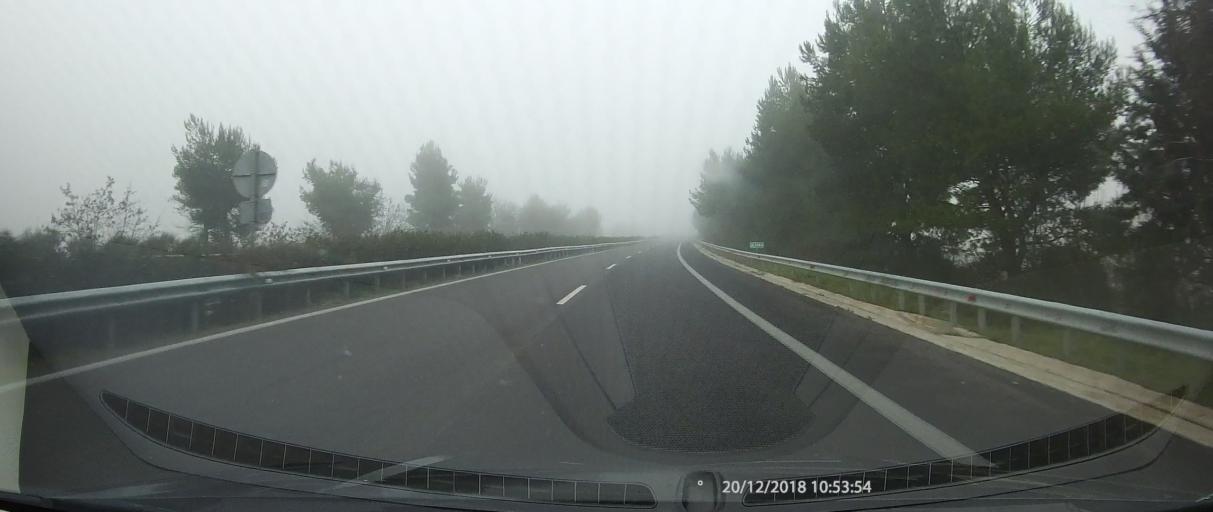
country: GR
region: Peloponnese
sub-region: Nomos Arkadias
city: Tripoli
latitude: 37.6176
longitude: 22.4586
